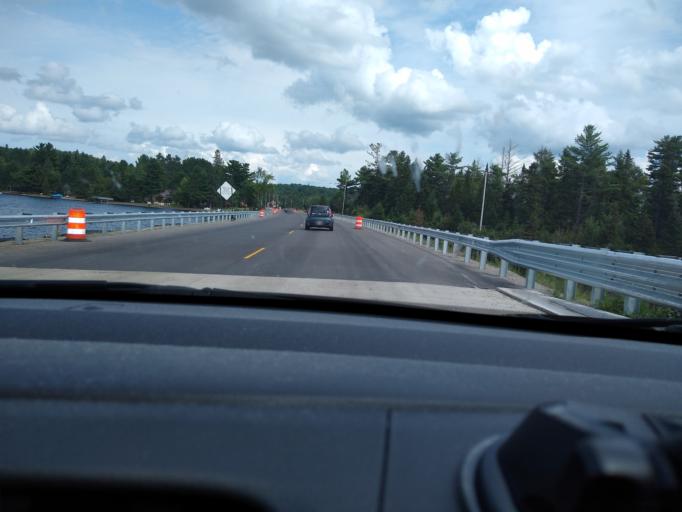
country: US
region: Michigan
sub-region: Baraga County
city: L'Anse
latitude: 46.5533
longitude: -88.2101
